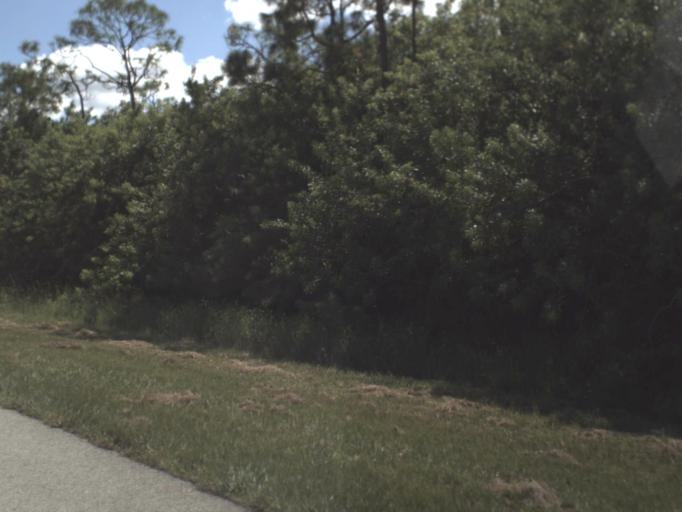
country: US
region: Florida
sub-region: Collier County
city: Lely Resort
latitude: 26.0076
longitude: -81.6123
